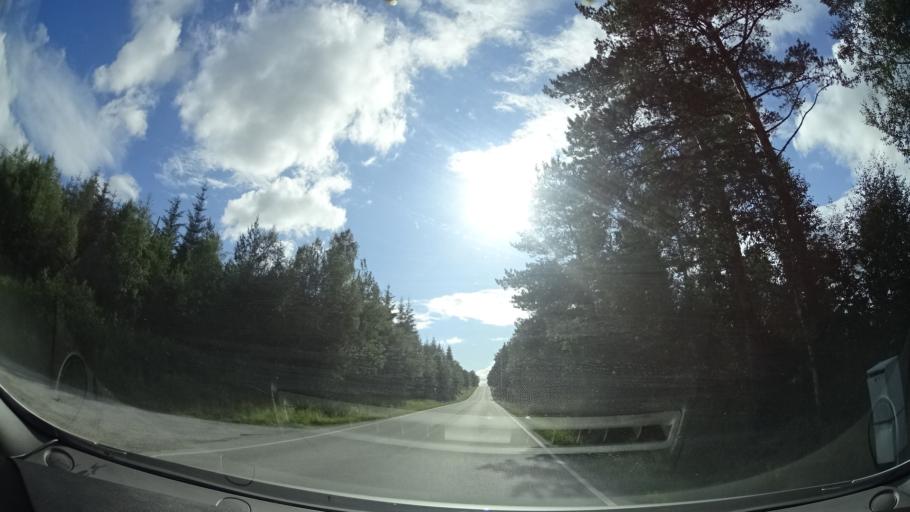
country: NO
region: More og Romsdal
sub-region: Halsa
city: Liaboen
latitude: 63.0733
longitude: 8.2974
